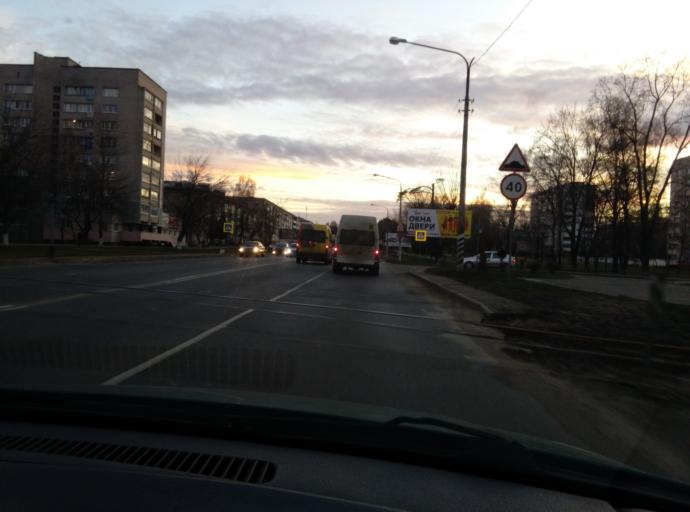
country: BY
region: Minsk
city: Horad Barysaw
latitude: 54.2176
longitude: 28.4903
